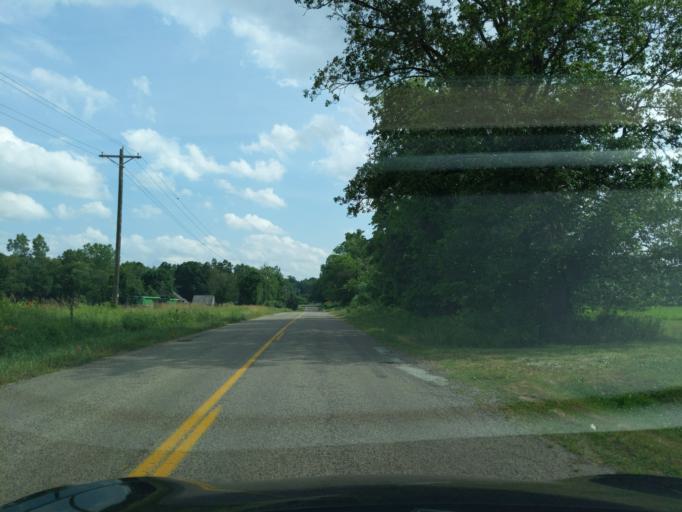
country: US
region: Michigan
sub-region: Eaton County
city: Eaton Rapids
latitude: 42.4979
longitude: -84.6305
